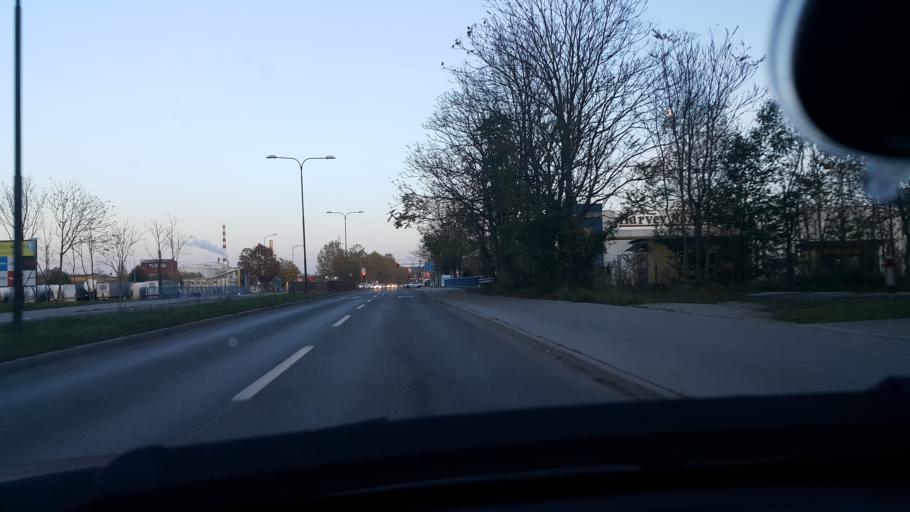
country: SI
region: Celje
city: Celje
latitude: 46.2352
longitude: 15.2779
